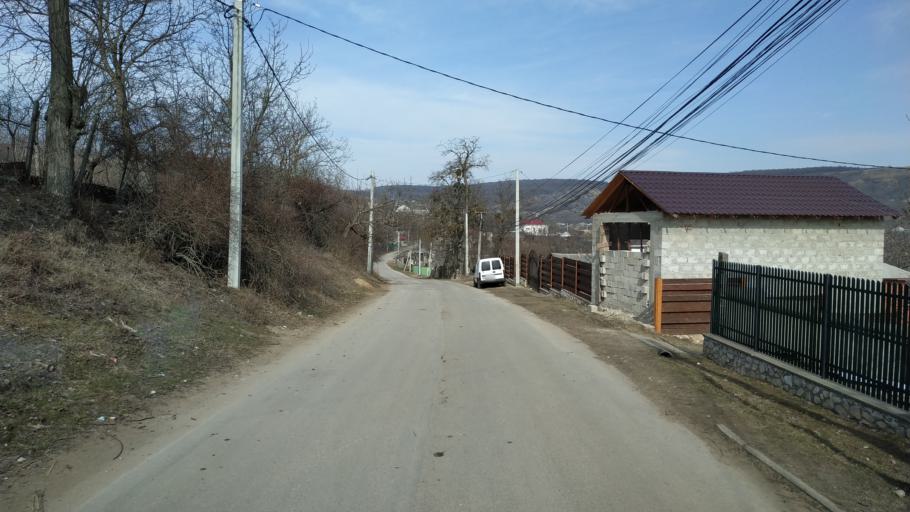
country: MD
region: Nisporeni
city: Nisporeni
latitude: 47.1975
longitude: 28.0653
